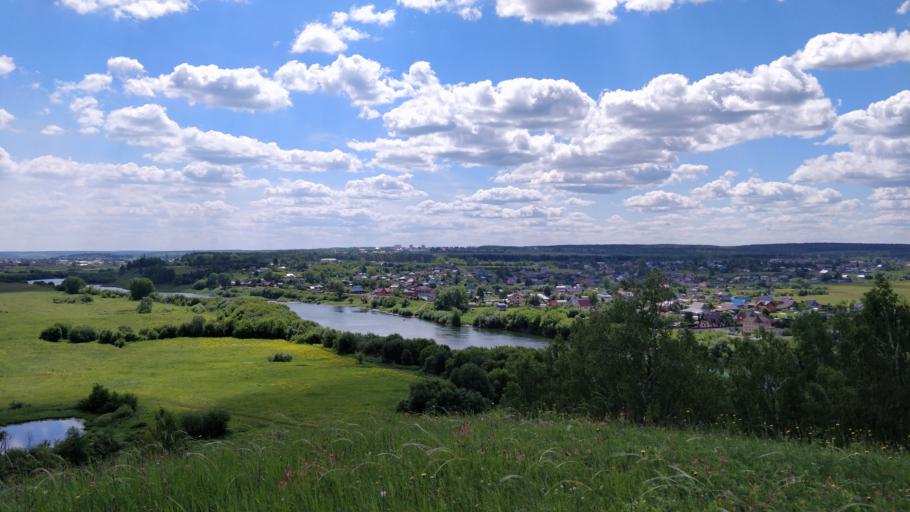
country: RU
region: Perm
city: Kungur
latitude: 57.4736
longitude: 56.9157
